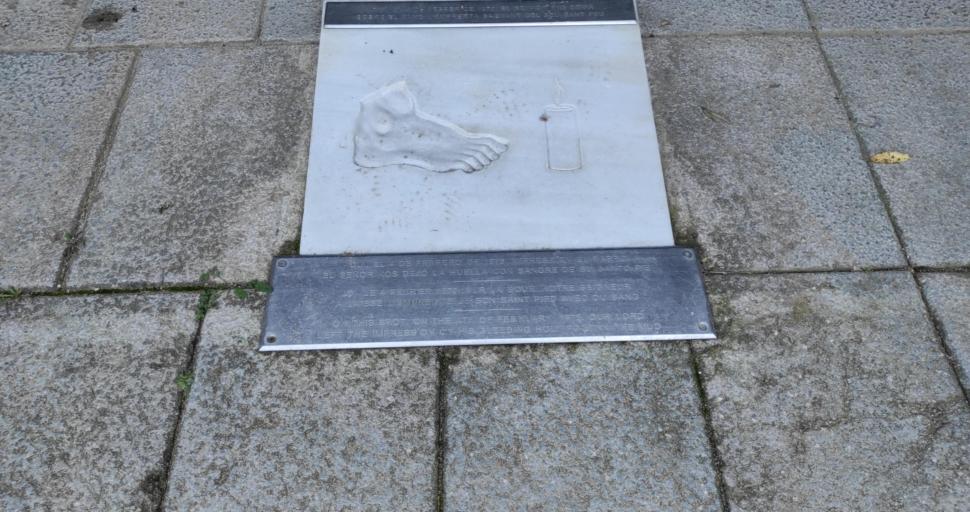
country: ES
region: Catalonia
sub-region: Provincia de Girona
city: Girona
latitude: 41.9868
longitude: 2.8293
